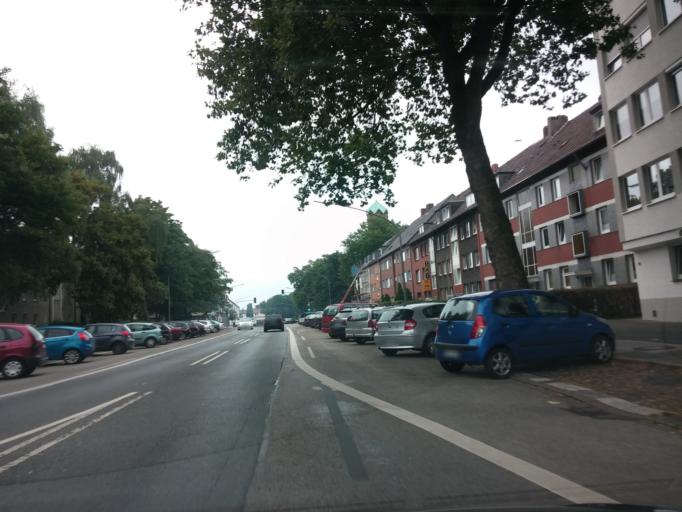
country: DE
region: North Rhine-Westphalia
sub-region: Regierungsbezirk Munster
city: Gladbeck
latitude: 51.5943
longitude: 7.0518
